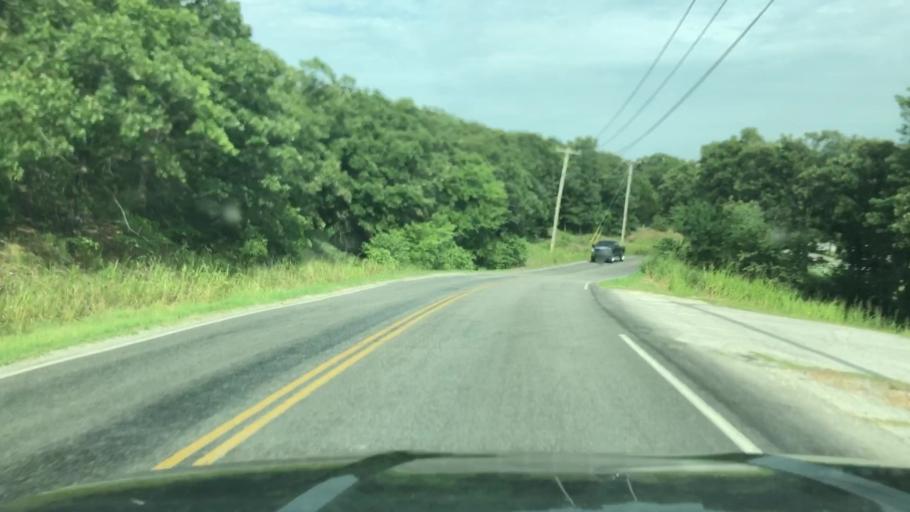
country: US
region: Oklahoma
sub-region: Tulsa County
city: Oakhurst
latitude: 36.0906
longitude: -96.0800
